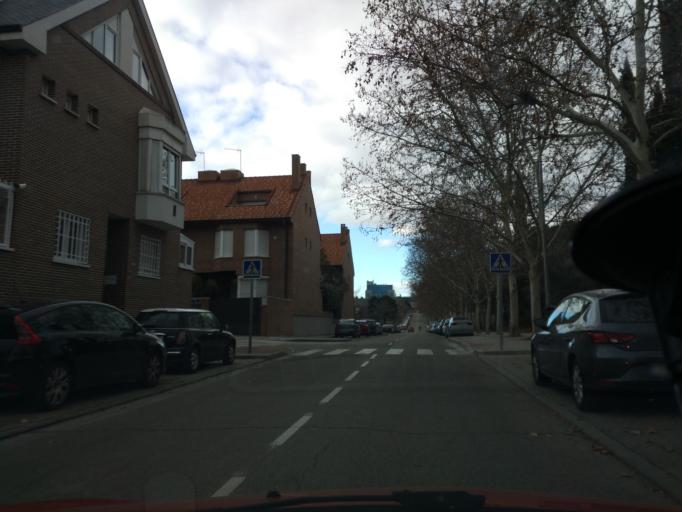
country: ES
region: Madrid
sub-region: Provincia de Madrid
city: San Blas
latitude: 40.4439
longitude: -3.6313
